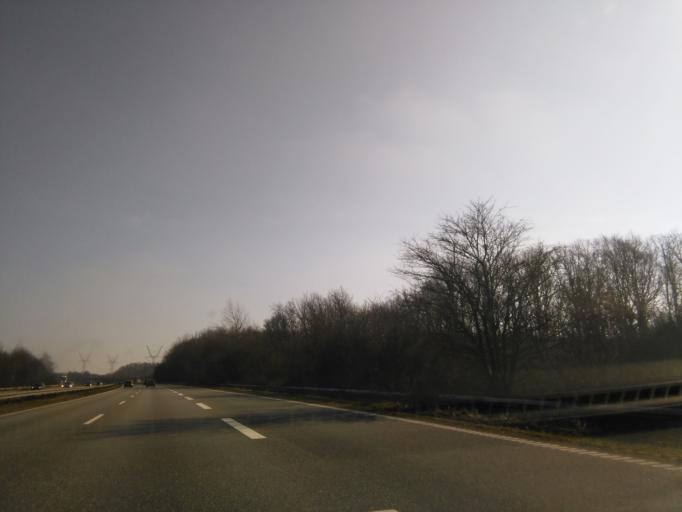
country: DK
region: South Denmark
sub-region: Assens Kommune
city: Arup
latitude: 55.4120
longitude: 10.0468
